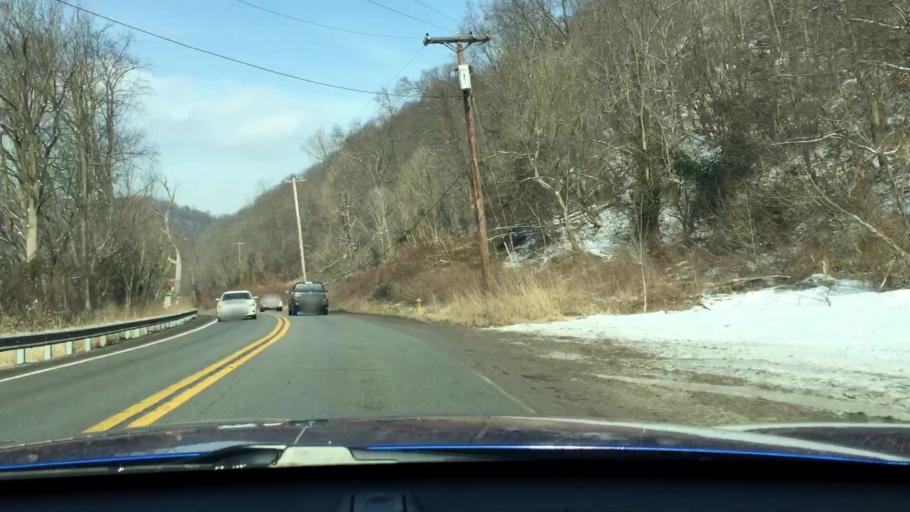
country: US
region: Pennsylvania
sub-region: Allegheny County
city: Clairton
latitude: 40.2939
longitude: -79.8648
